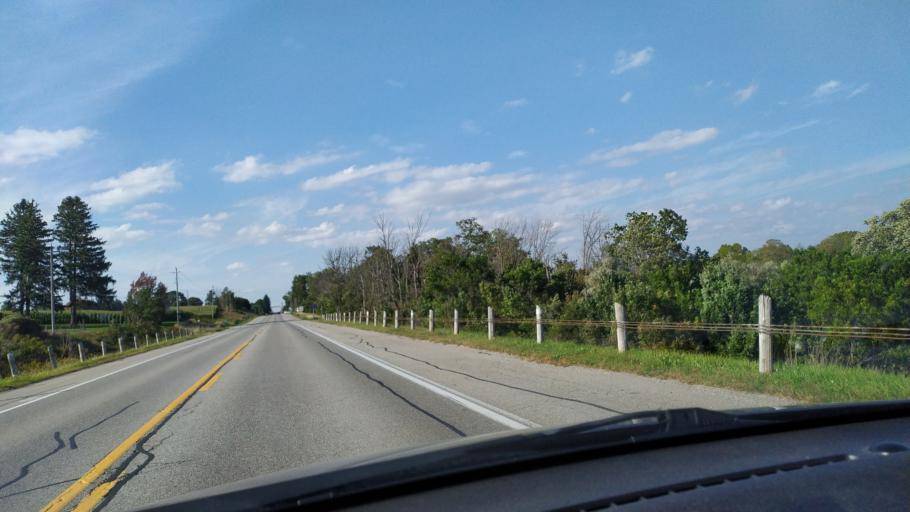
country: CA
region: Ontario
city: Ingersoll
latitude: 43.1459
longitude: -80.8962
